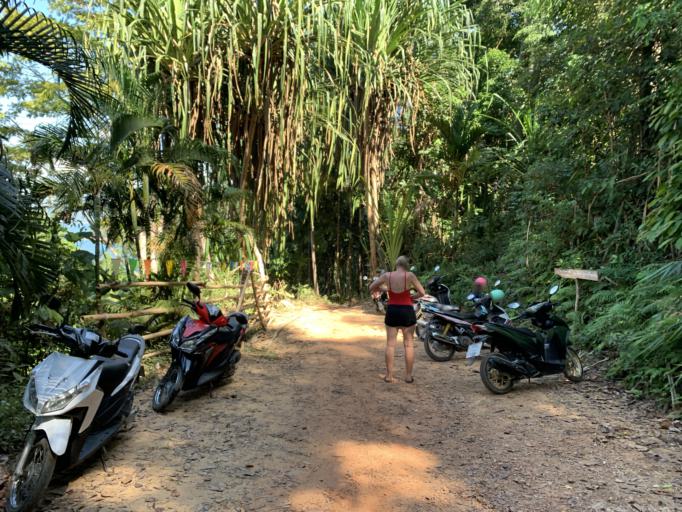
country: TH
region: Ranong
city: Kapoe
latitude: 9.7694
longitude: 98.4104
